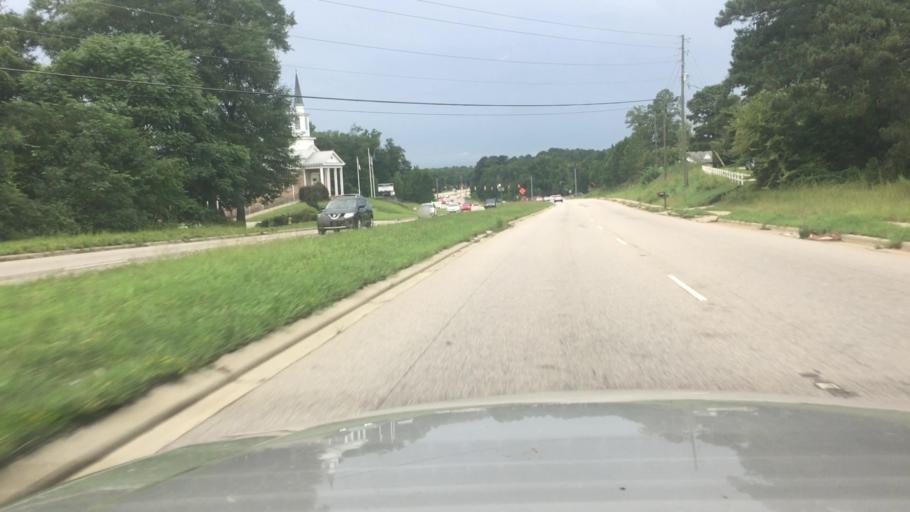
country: US
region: North Carolina
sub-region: Cumberland County
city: Hope Mills
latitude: 34.9996
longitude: -78.9736
